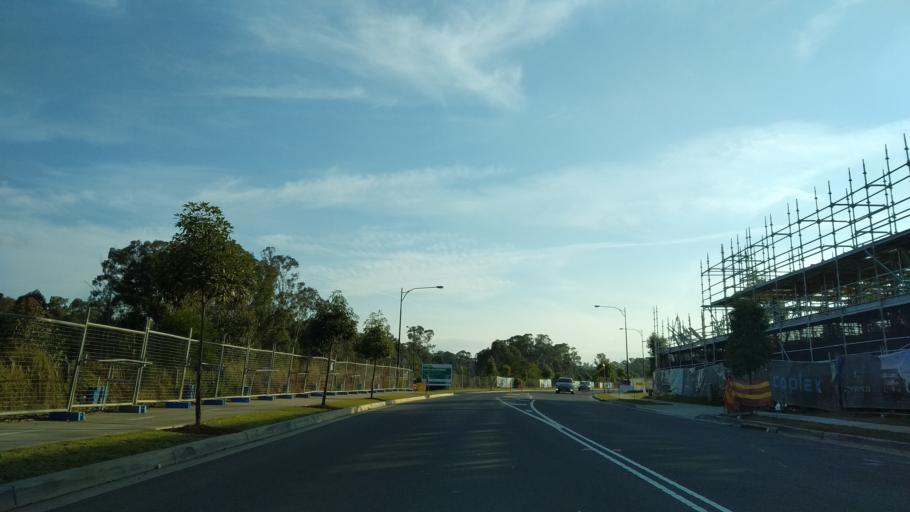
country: AU
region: New South Wales
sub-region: Penrith Municipality
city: Werrington Downs
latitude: -33.7287
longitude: 150.7284
